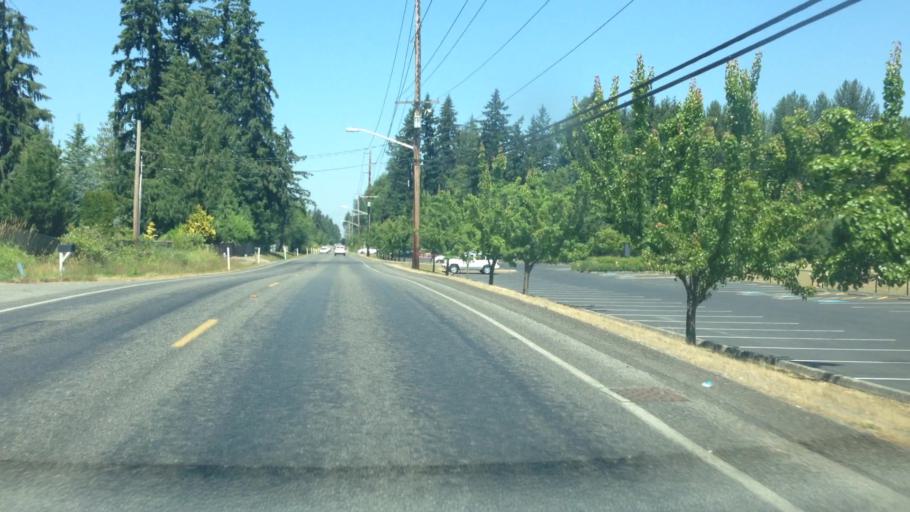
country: US
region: Washington
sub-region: Pierce County
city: South Hill
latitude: 47.1266
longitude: -122.3149
